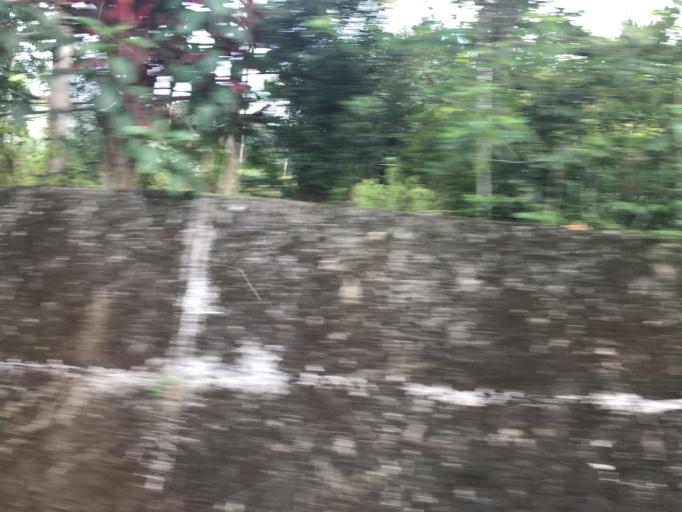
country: TW
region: Taiwan
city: Daxi
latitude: 24.9155
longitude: 121.3491
